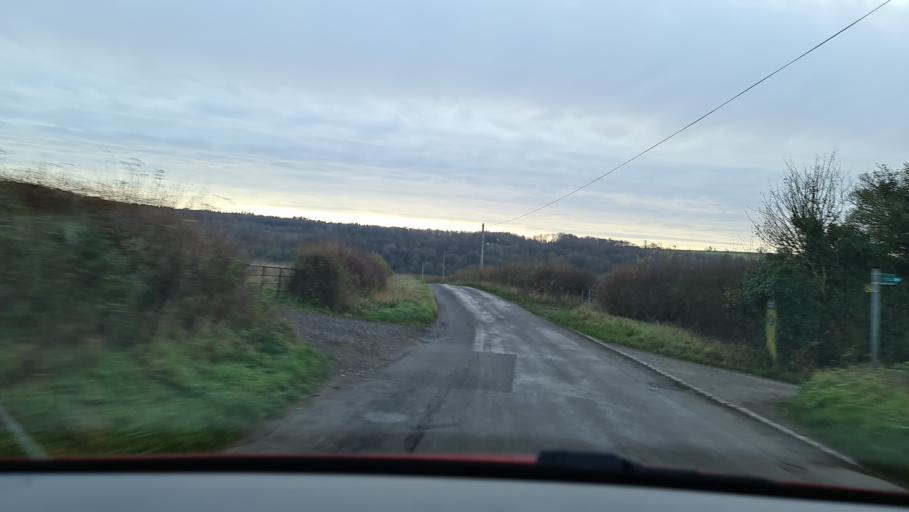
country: GB
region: England
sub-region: Buckinghamshire
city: Princes Risborough
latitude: 51.7172
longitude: -0.8194
